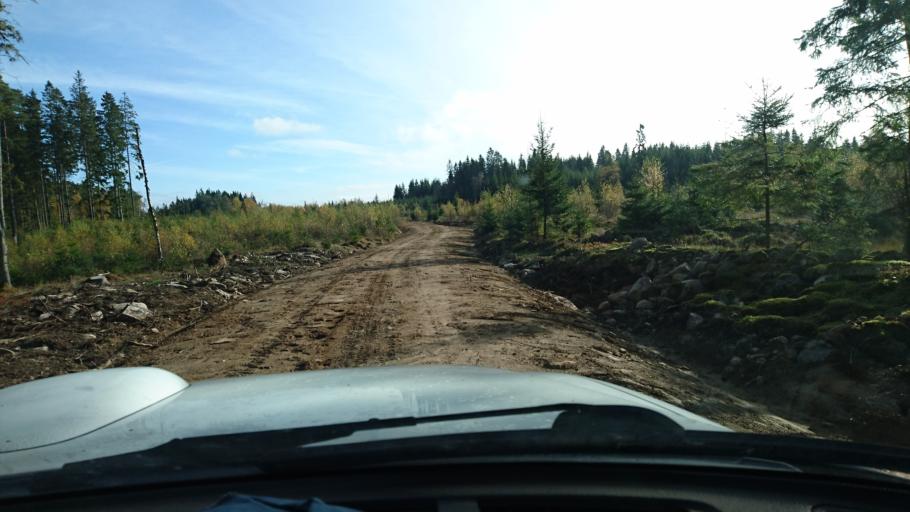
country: SE
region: Vaestra Goetaland
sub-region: Ulricehamns Kommun
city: Ulricehamn
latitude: 57.9368
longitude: 13.5581
